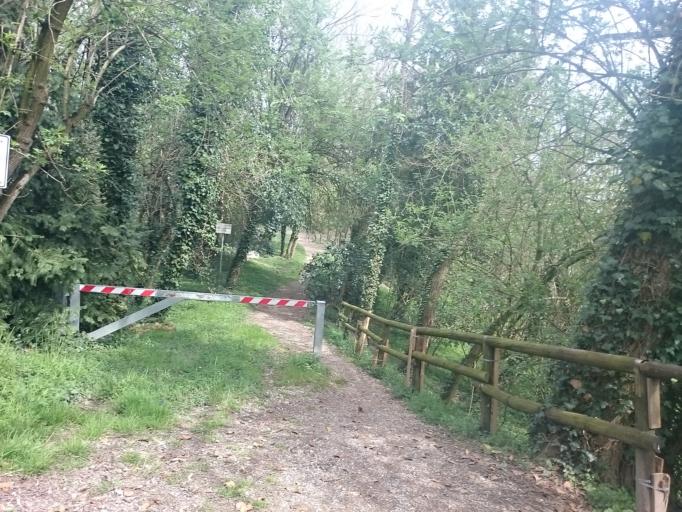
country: IT
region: Veneto
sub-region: Provincia di Padova
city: Limena
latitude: 45.4830
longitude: 11.8443
